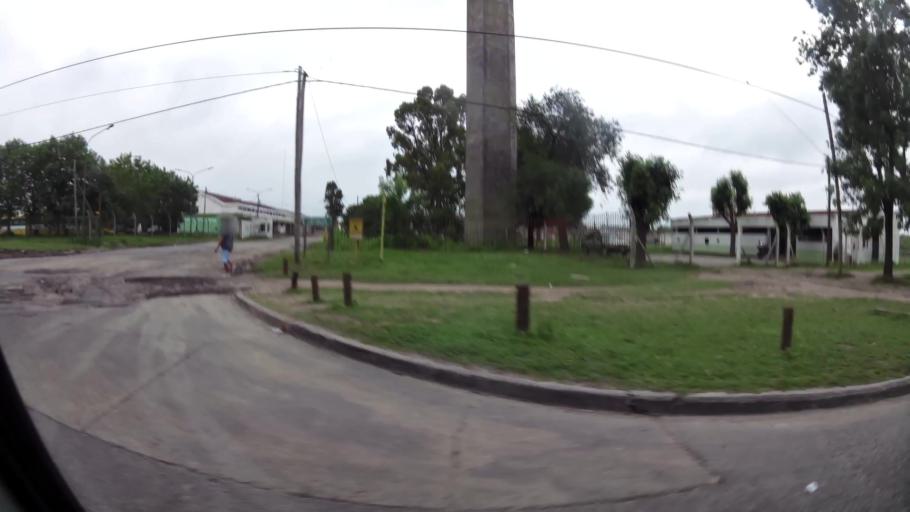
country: AR
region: Buenos Aires
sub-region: Partido de La Plata
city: La Plata
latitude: -34.8813
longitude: -57.9728
